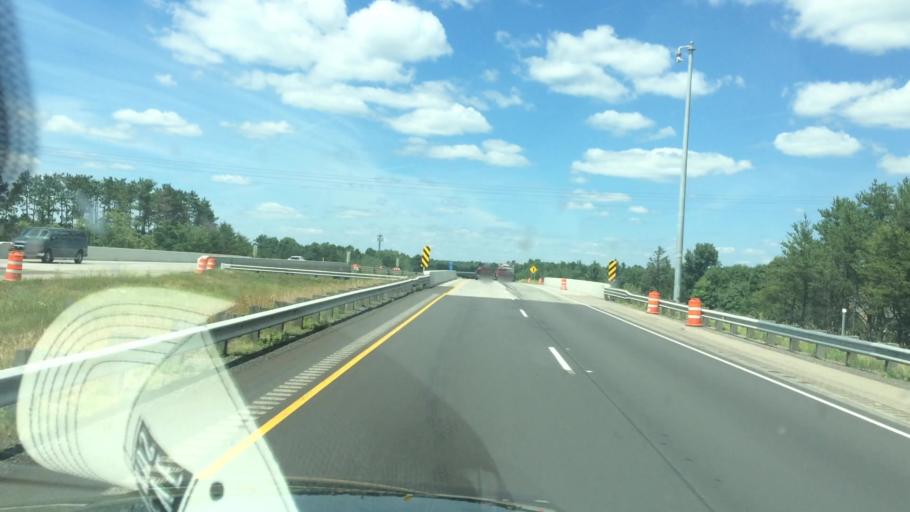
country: US
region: Wisconsin
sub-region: Portage County
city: Stevens Point
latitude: 44.5402
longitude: -89.5436
